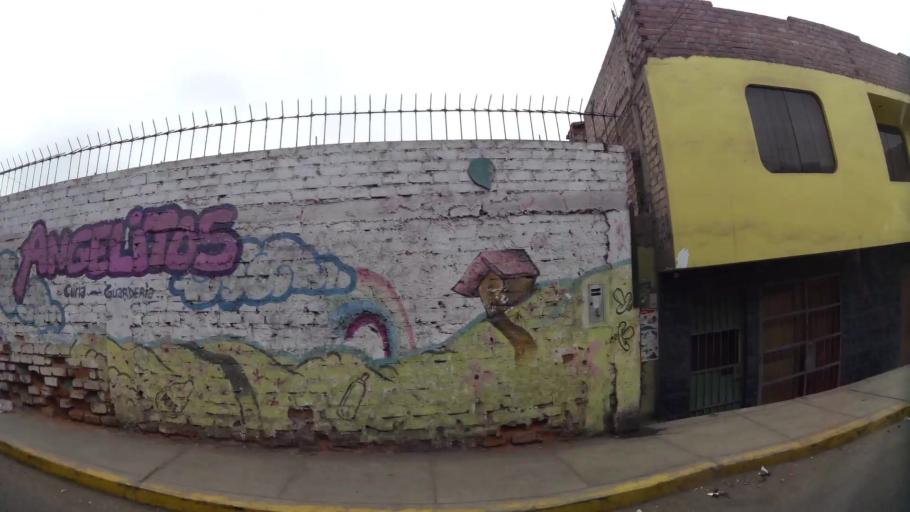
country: PE
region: Lima
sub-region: Lima
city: Surco
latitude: -12.1886
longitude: -77.0142
